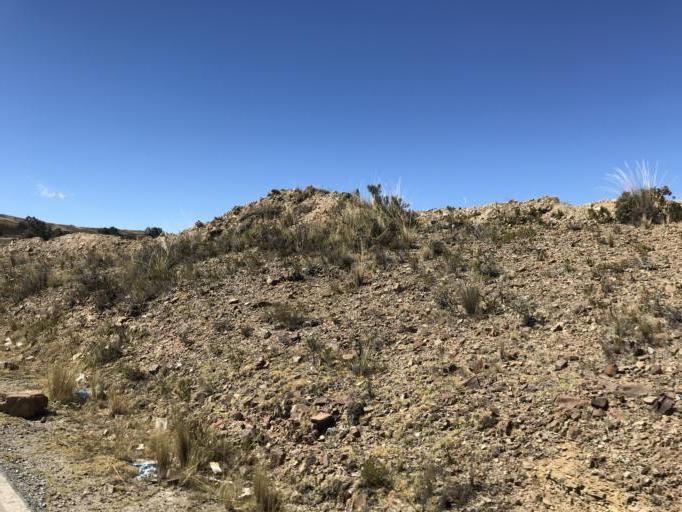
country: BO
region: La Paz
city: San Pablo
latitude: -16.2005
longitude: -68.8313
